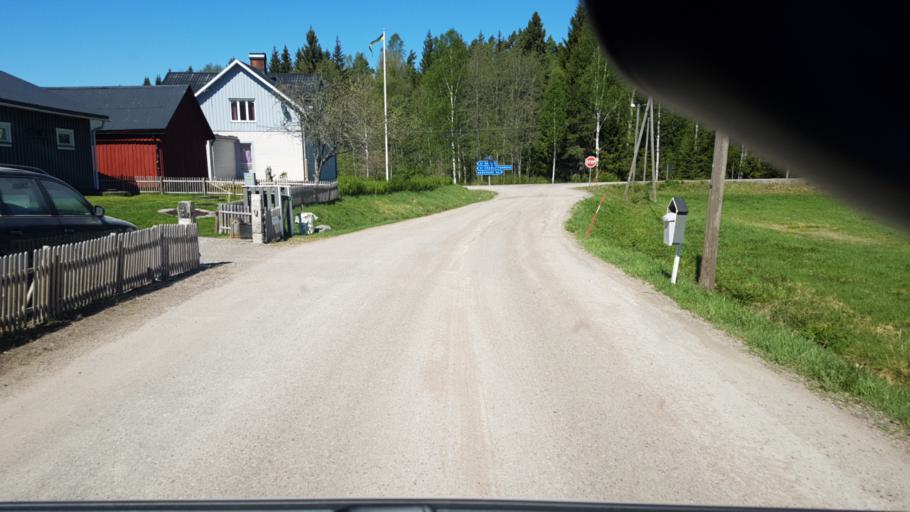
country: SE
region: Vaermland
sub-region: Arvika Kommun
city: Arvika
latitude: 59.8747
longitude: 12.6125
